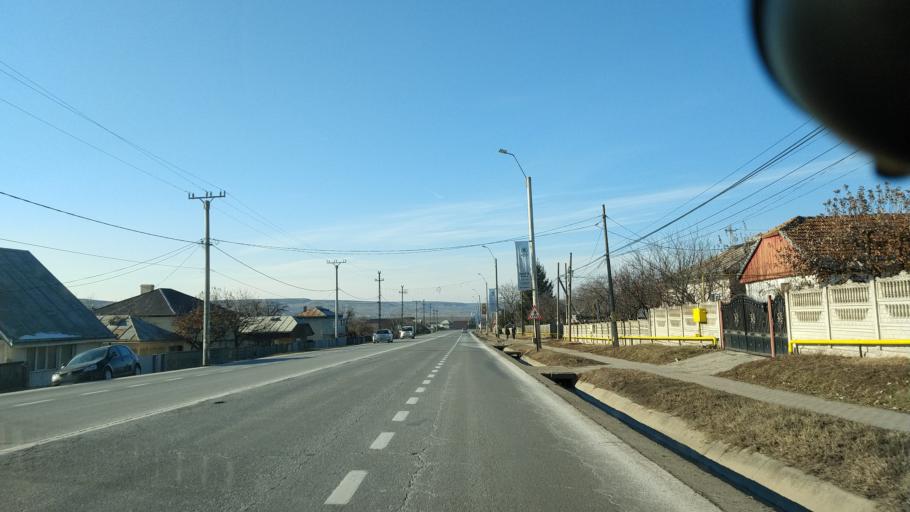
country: RO
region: Iasi
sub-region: Comuna Letcani
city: Letcani
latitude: 47.1956
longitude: 27.4035
